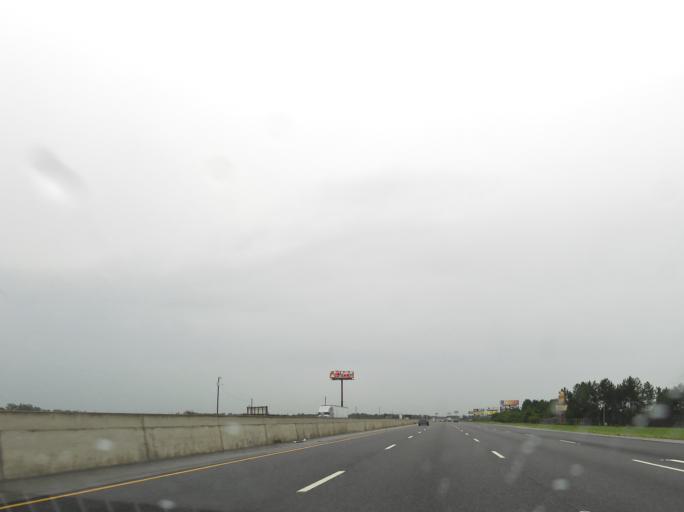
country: US
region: Georgia
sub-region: Turner County
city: Ashburn
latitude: 31.7079
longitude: -83.6356
